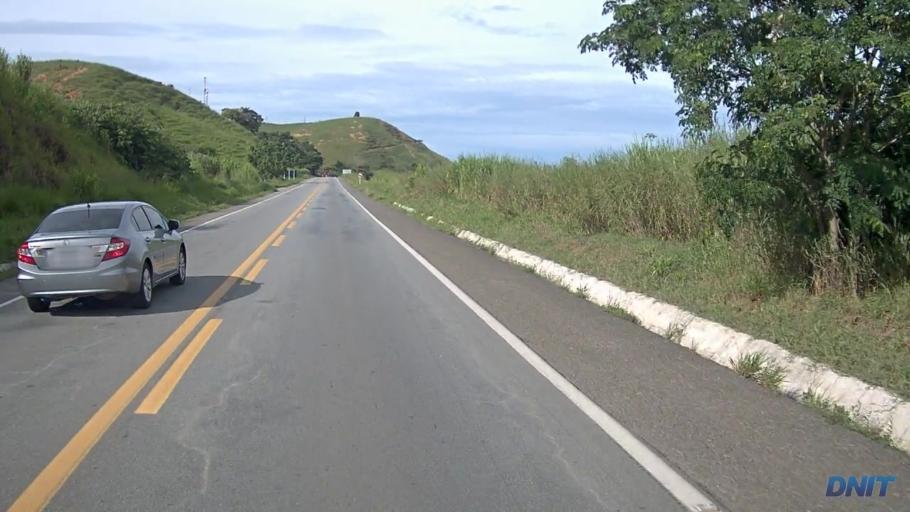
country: BR
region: Minas Gerais
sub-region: Belo Oriente
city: Belo Oriente
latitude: -19.1703
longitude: -42.2481
